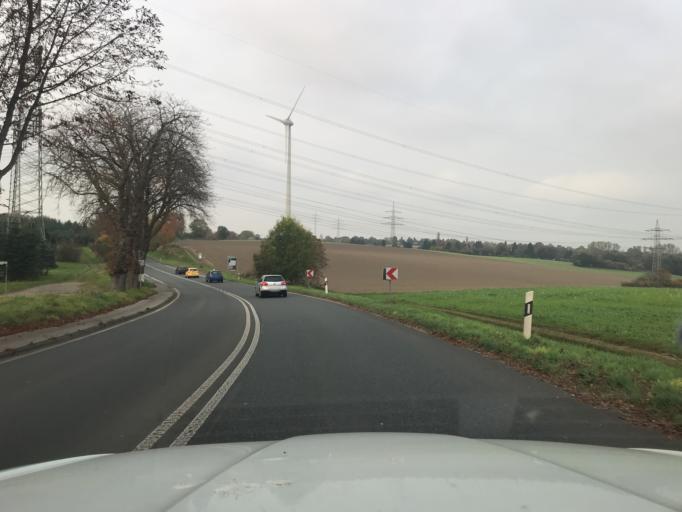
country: DE
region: North Rhine-Westphalia
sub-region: Regierungsbezirk Dusseldorf
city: Velbert
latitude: 51.3590
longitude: 7.0210
